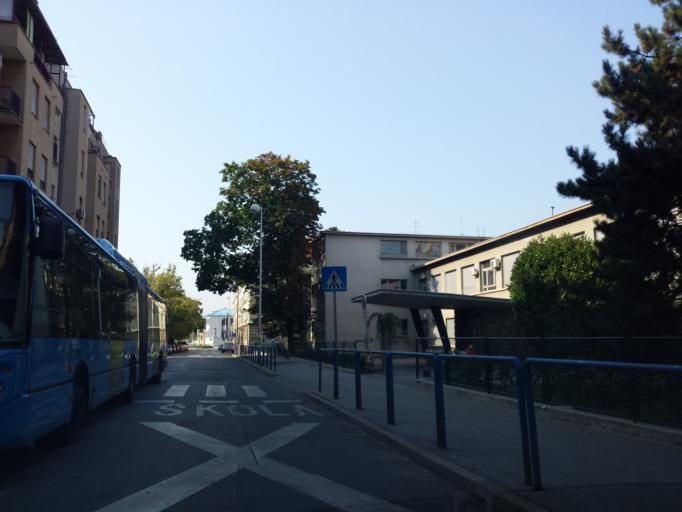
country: HR
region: Grad Zagreb
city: Zagreb - Centar
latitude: 45.8135
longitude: 15.9384
